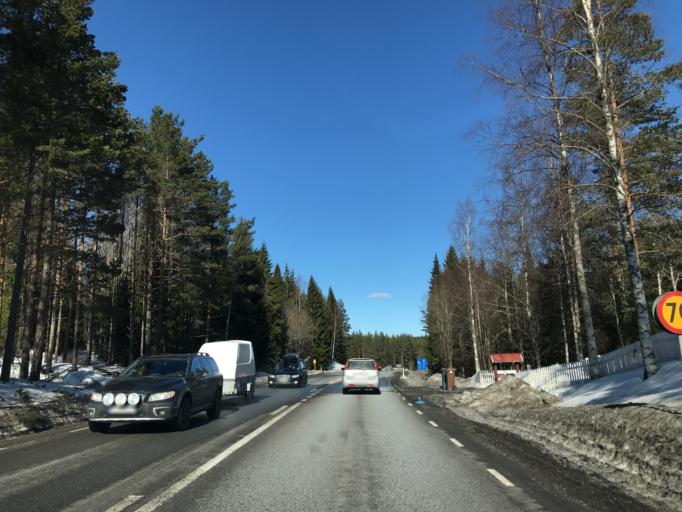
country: SE
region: Vaermland
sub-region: Filipstads Kommun
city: Filipstad
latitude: 59.7674
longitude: 14.2592
